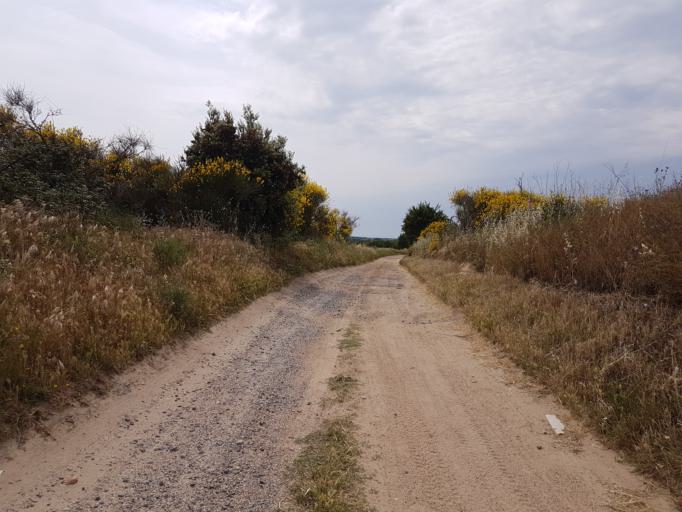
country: FR
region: Languedoc-Roussillon
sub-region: Departement de l'Herault
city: Vias
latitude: 43.3110
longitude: 3.3761
